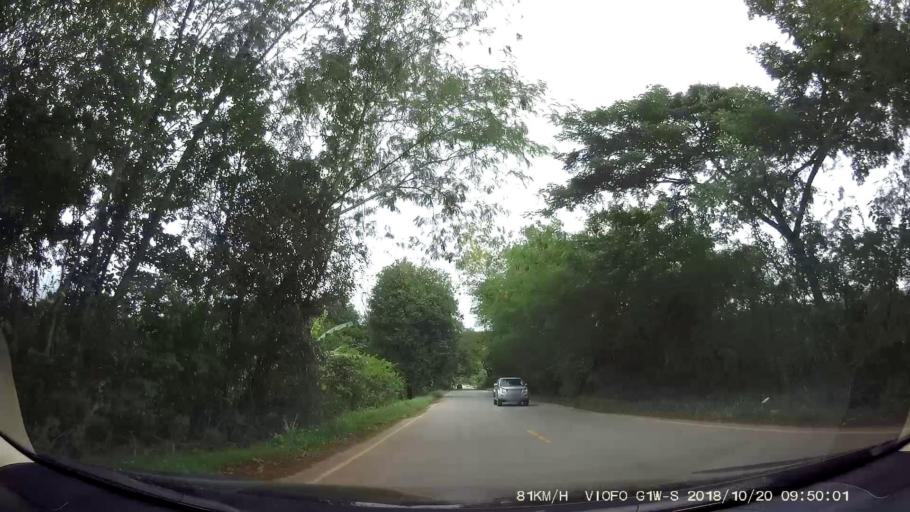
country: TH
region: Chaiyaphum
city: Khon San
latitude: 16.5264
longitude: 101.9034
